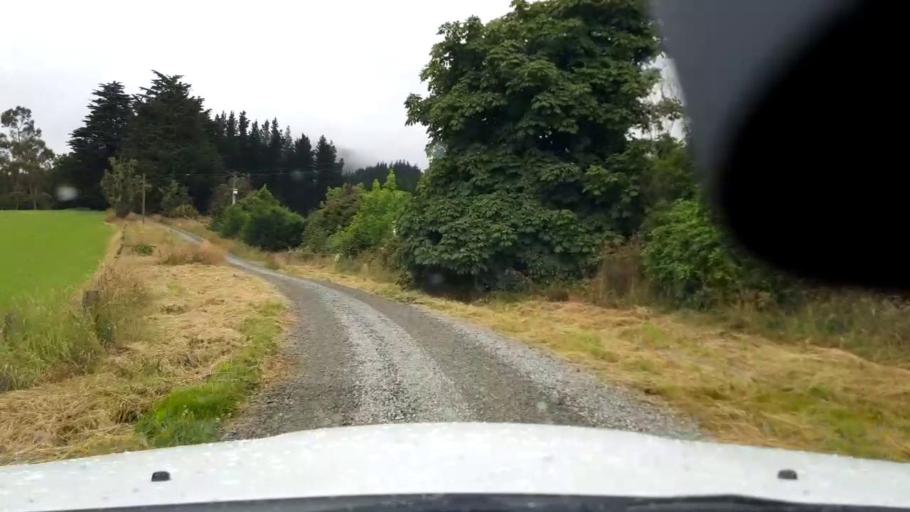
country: NZ
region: Canterbury
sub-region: Timaru District
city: Pleasant Point
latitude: -44.0772
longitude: 171.1404
